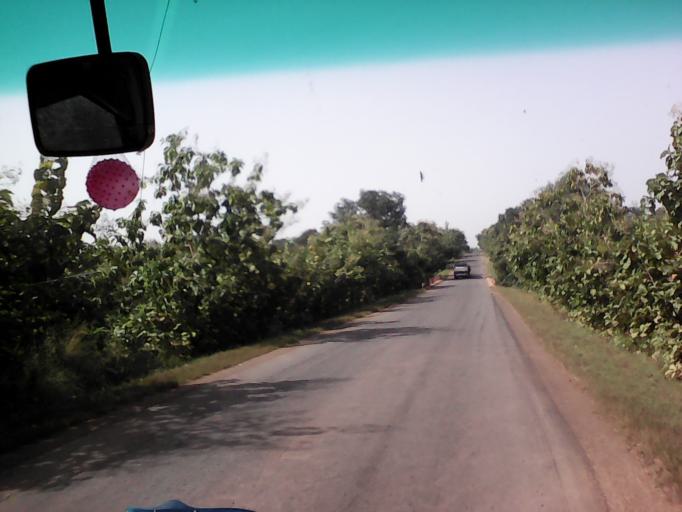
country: TG
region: Centrale
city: Sokode
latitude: 8.9074
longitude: 1.0969
